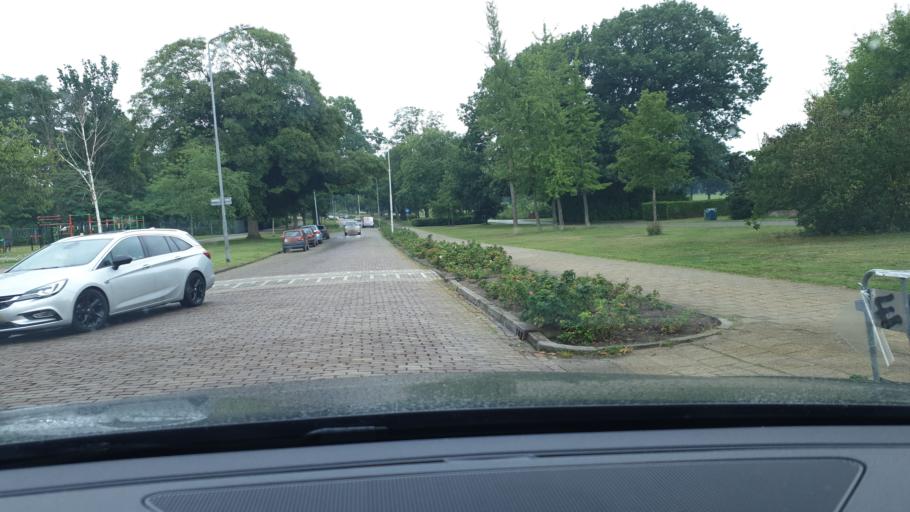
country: NL
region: Gelderland
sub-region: Gemeente Nijmegen
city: Nijmegen
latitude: 51.8283
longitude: 5.8363
